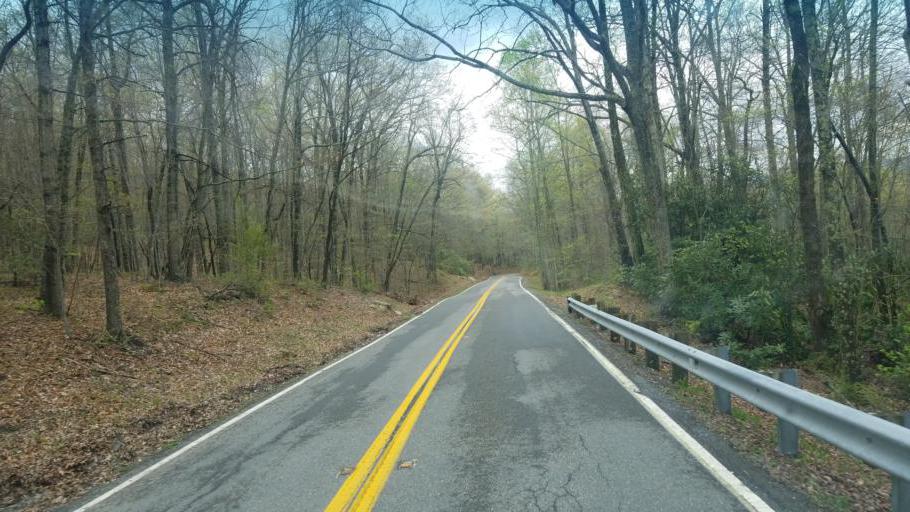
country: US
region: Virginia
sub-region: Tazewell County
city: Tazewell
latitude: 36.9942
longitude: -81.5329
